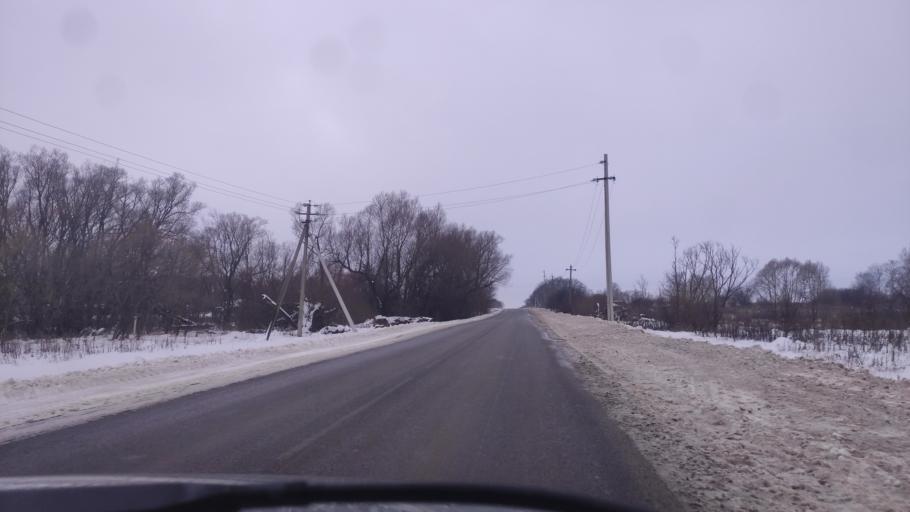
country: RU
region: Tambov
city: Pervomayskiy
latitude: 53.3027
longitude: 40.3740
